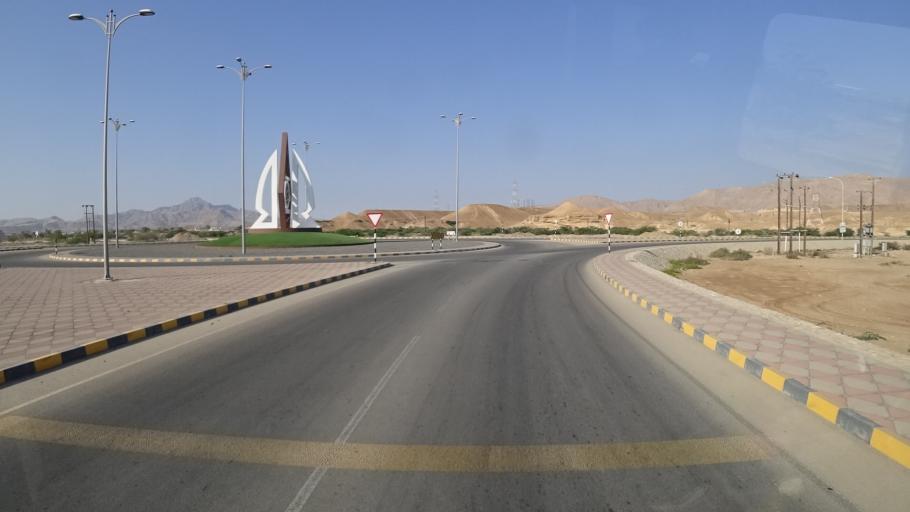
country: OM
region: Ash Sharqiyah
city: Sur
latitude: 22.5748
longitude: 59.4665
